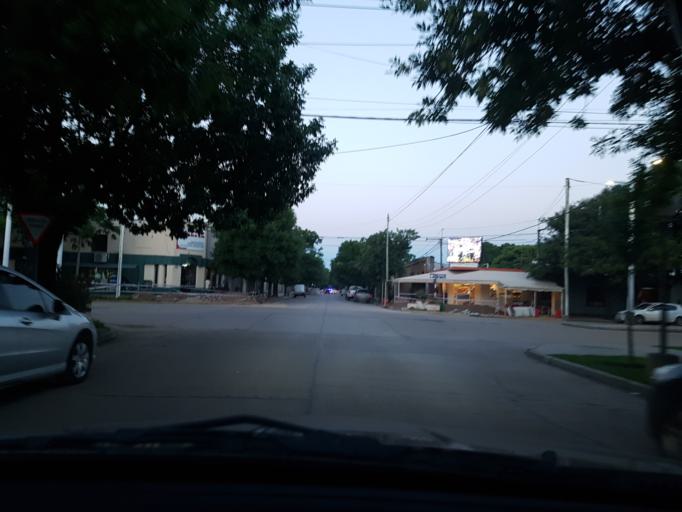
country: AR
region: Cordoba
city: General Cabrera
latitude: -32.7550
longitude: -63.7900
